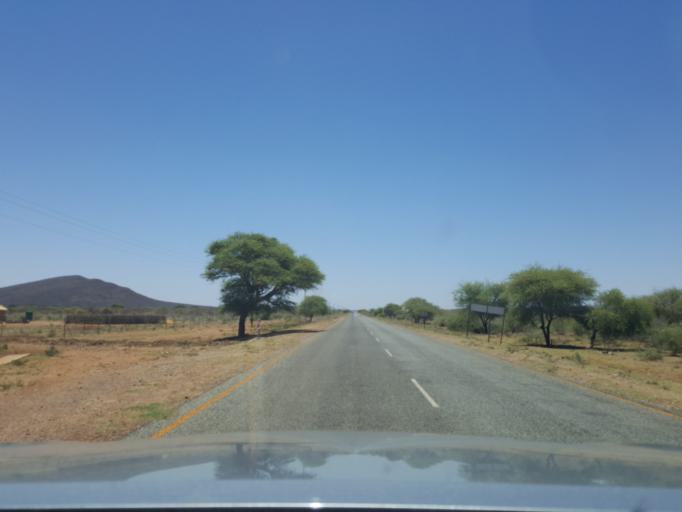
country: BW
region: South East
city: Ramotswa
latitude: -24.9581
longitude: 25.8954
